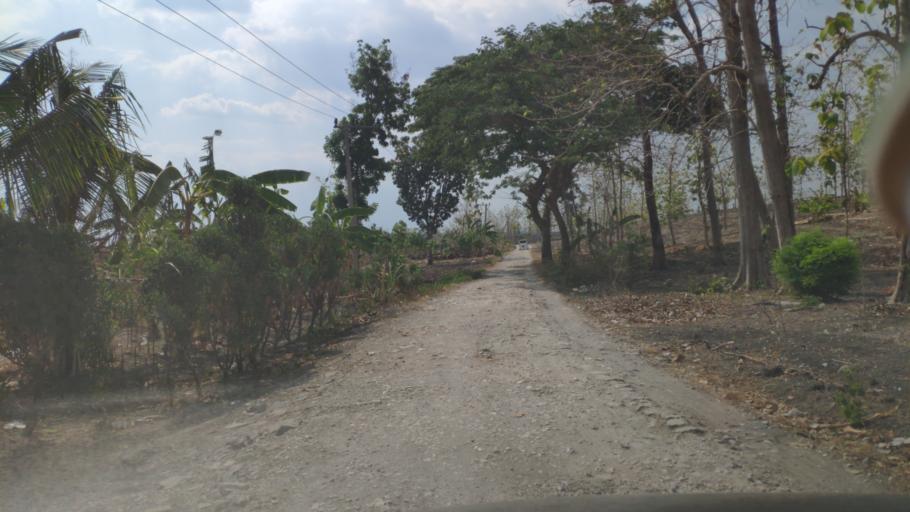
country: ID
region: Central Java
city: Mendenrejo
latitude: -7.3192
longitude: 111.3778
